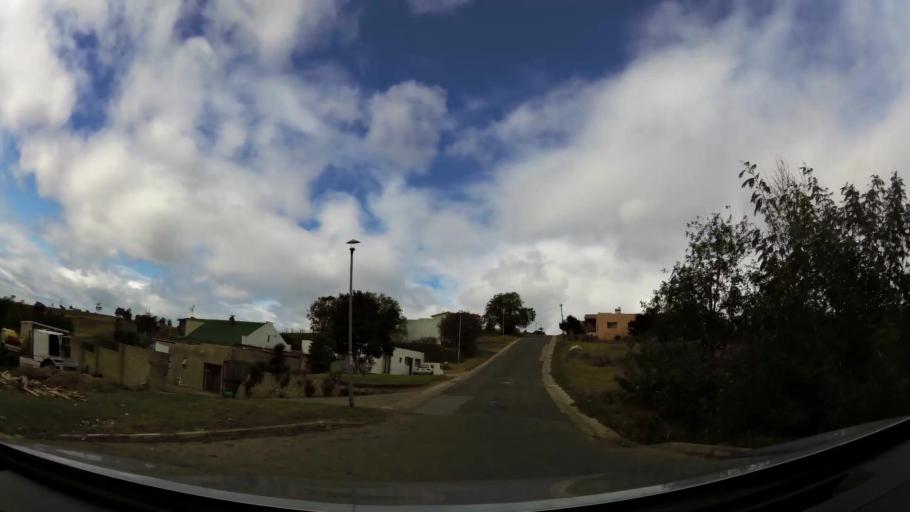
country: ZA
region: Western Cape
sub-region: Eden District Municipality
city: George
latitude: -34.0117
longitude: 22.4598
